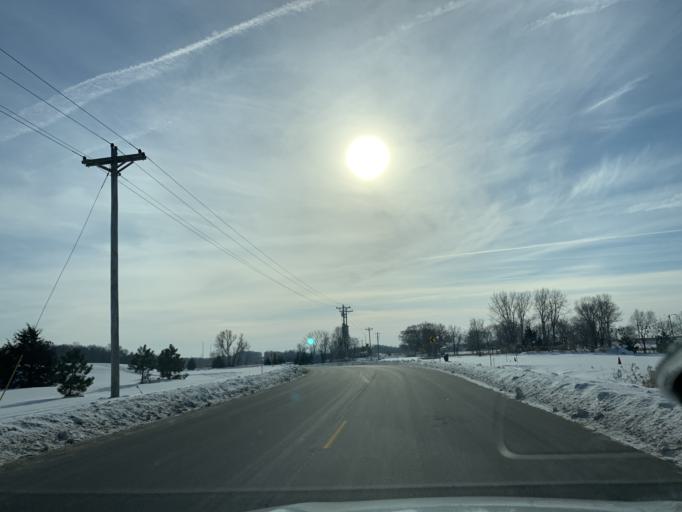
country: US
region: Minnesota
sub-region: Anoka County
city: Columbus
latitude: 45.2530
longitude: -93.0216
